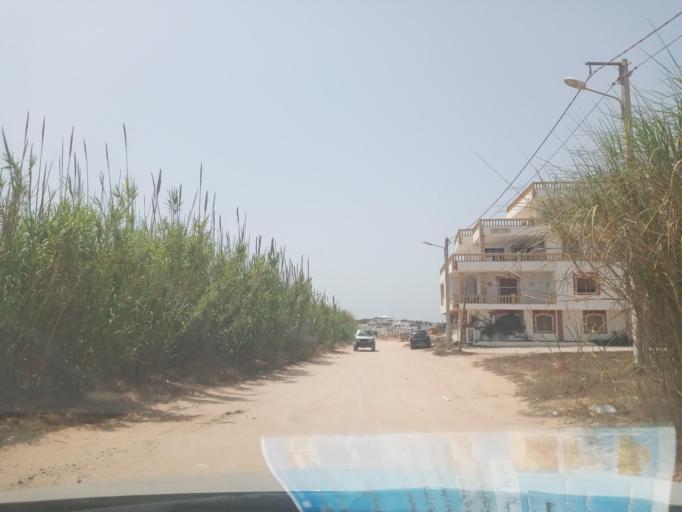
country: TN
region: Nabul
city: El Haouaria
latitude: 37.0315
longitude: 11.0570
